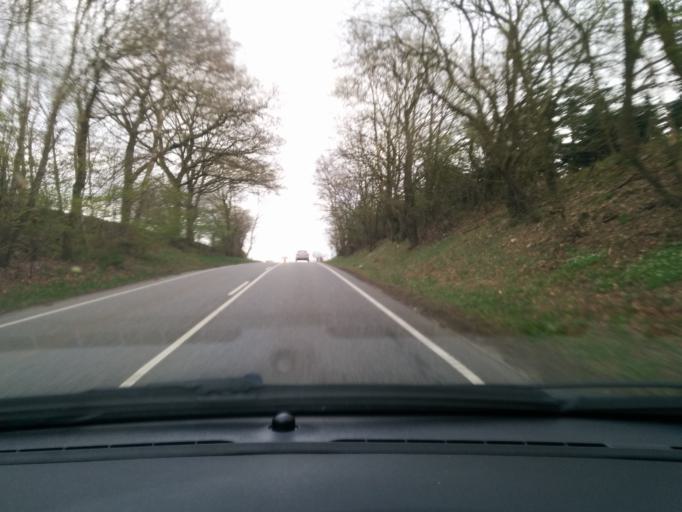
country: DK
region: Central Jutland
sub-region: Favrskov Kommune
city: Hammel
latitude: 56.2110
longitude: 9.7986
